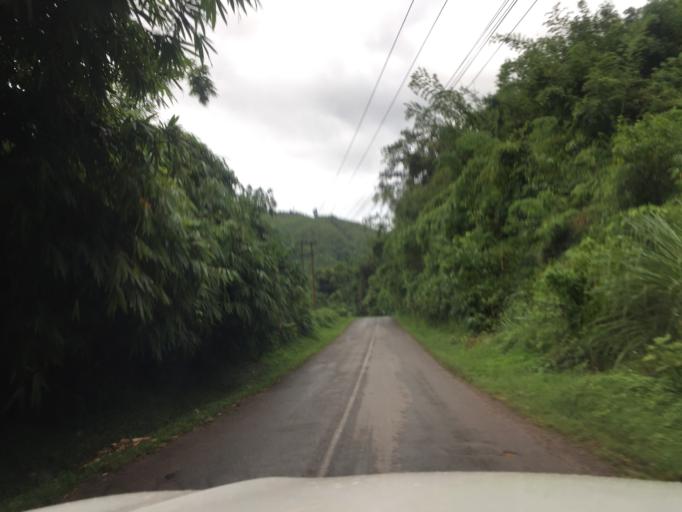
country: LA
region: Oudomxai
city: Muang La
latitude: 20.7941
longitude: 102.0855
